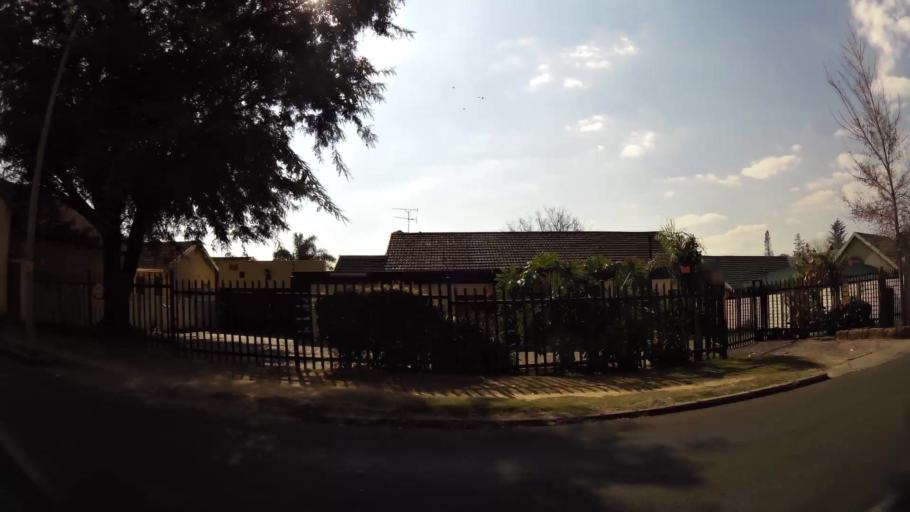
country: ZA
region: Gauteng
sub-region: City of Johannesburg Metropolitan Municipality
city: Modderfontein
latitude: -26.0946
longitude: 28.2452
